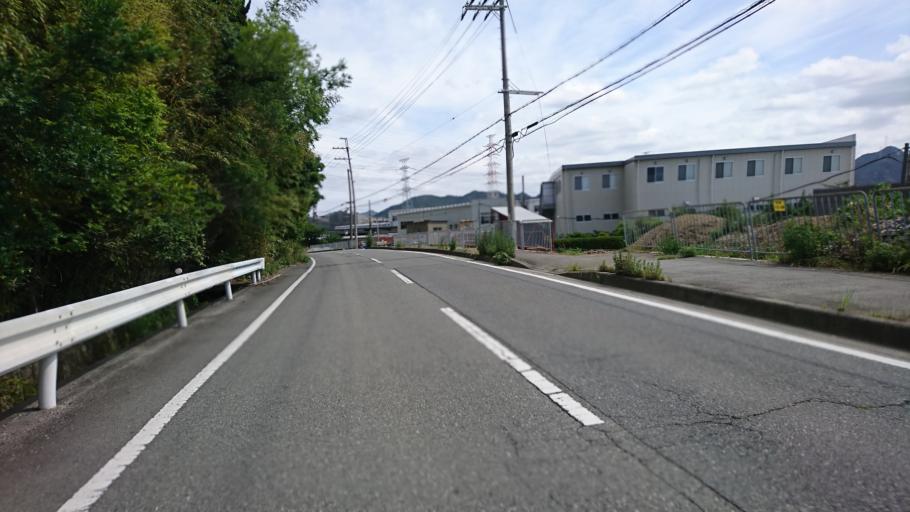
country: JP
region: Hyogo
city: Shirahamacho-usazakiminami
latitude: 34.8053
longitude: 134.7441
